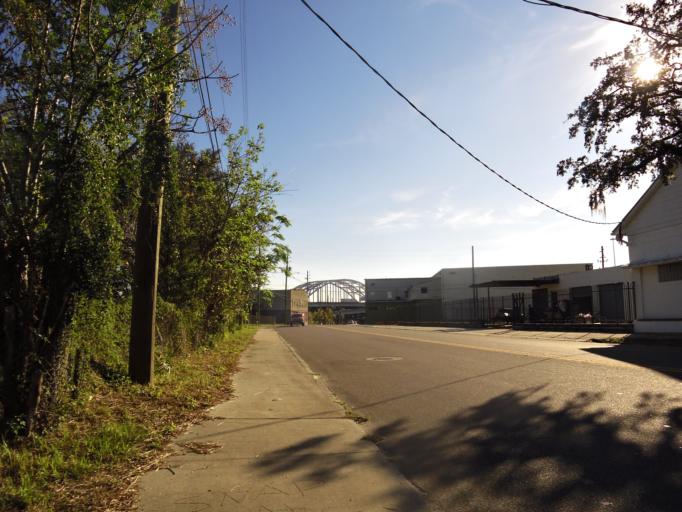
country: US
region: Florida
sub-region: Duval County
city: Jacksonville
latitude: 30.3325
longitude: -81.6759
